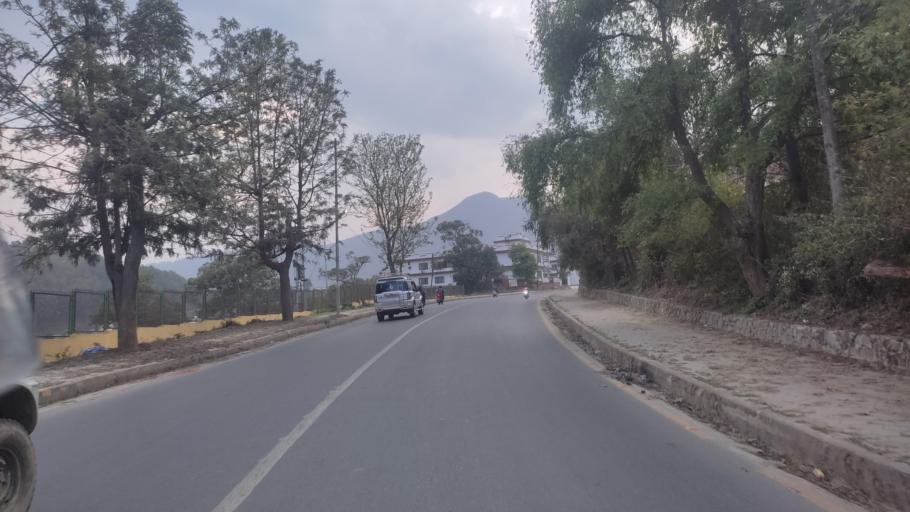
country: NP
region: Central Region
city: Kirtipur
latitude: 27.6759
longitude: 85.2910
